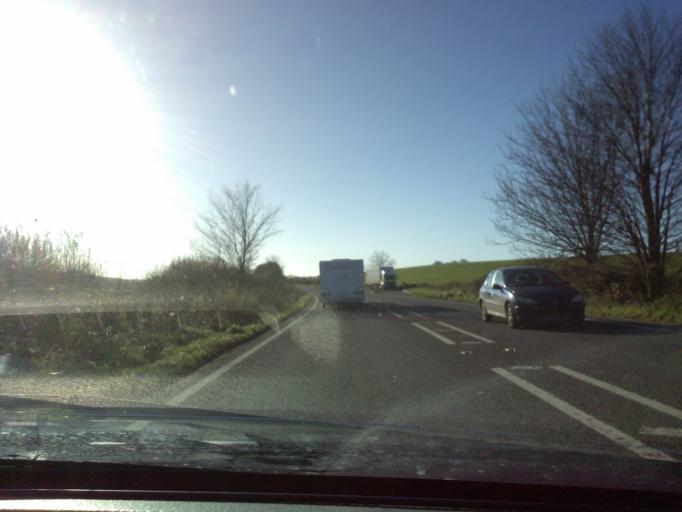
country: GB
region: England
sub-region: Dorset
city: Bovington Camp
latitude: 50.7620
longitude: -2.2080
